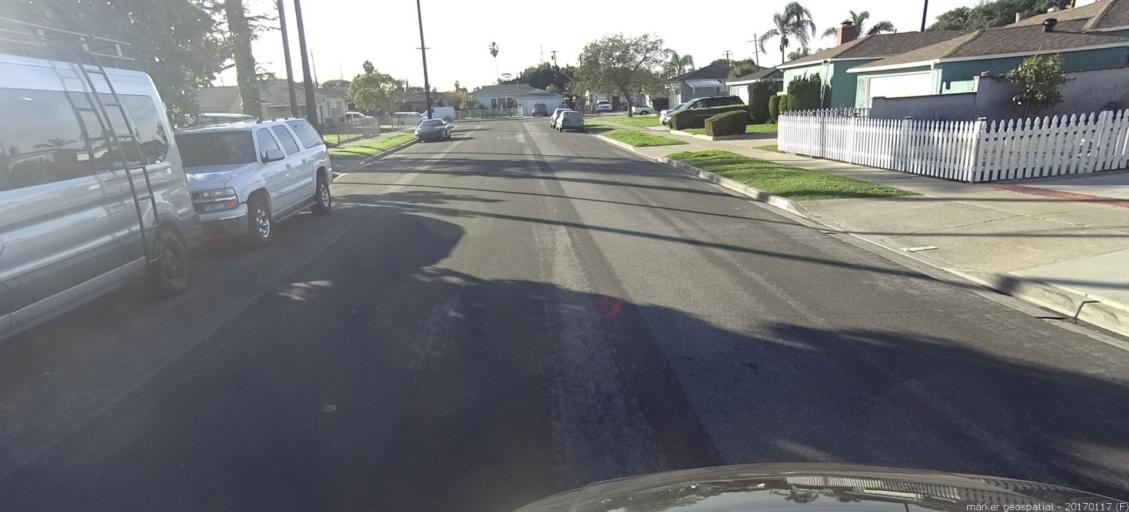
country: US
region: California
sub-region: Orange County
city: Midway City
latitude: 33.7407
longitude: -117.9924
